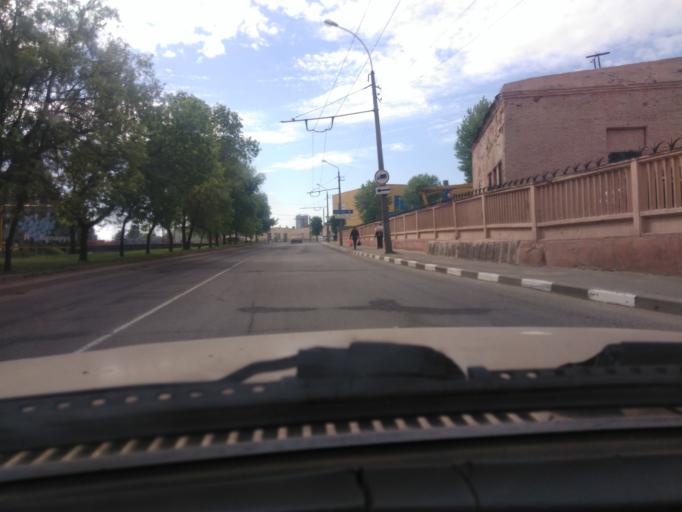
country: BY
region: Mogilev
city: Buynichy
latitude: 53.8929
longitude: 30.2984
